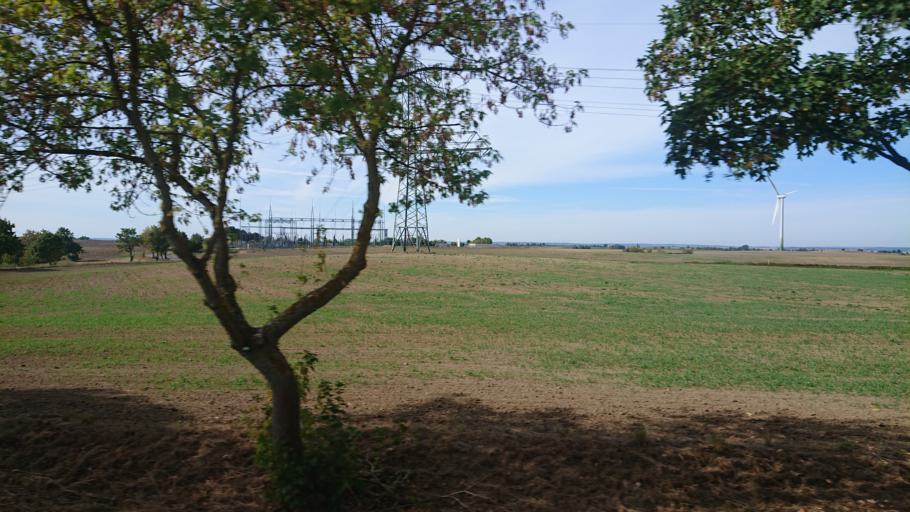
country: DE
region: Brandenburg
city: Gramzow
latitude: 53.2539
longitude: 13.9619
